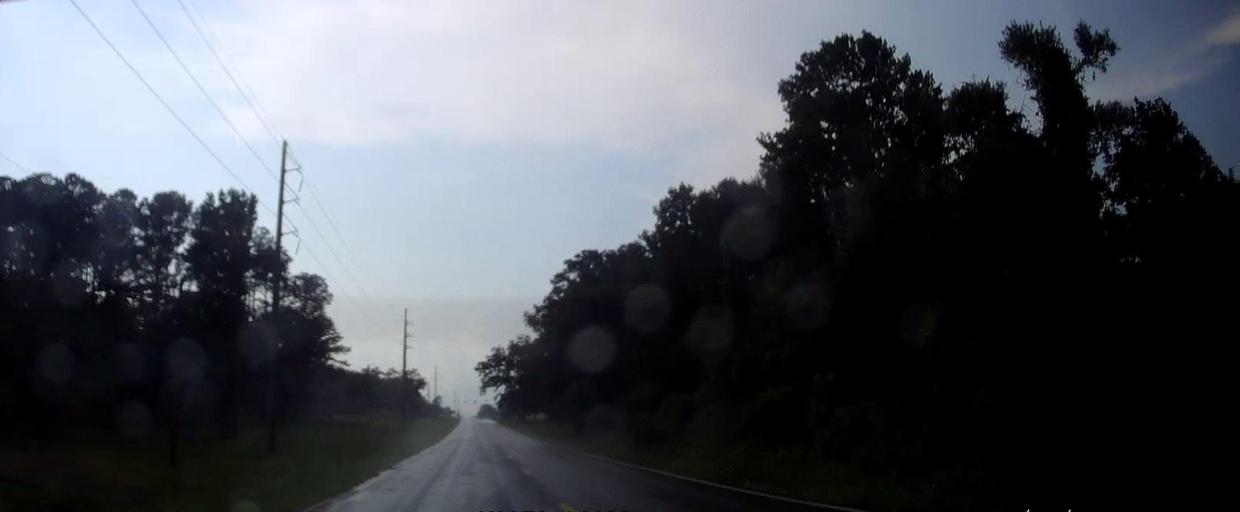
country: US
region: Georgia
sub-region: Twiggs County
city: Jeffersonville
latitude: 32.5889
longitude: -83.2255
